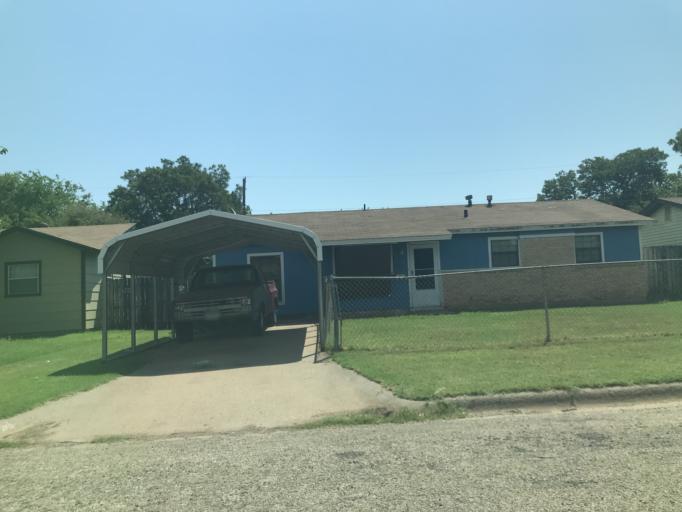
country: US
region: Texas
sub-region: Taylor County
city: Abilene
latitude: 32.4728
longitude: -99.7674
